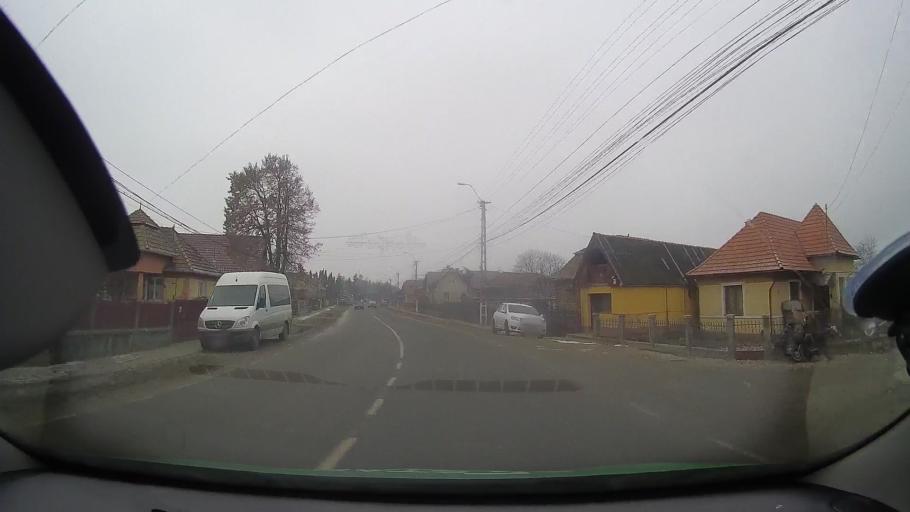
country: RO
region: Cluj
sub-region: Comuna Mihai Viteazu
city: Mihai Viteazu
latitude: 46.5410
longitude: 23.7494
